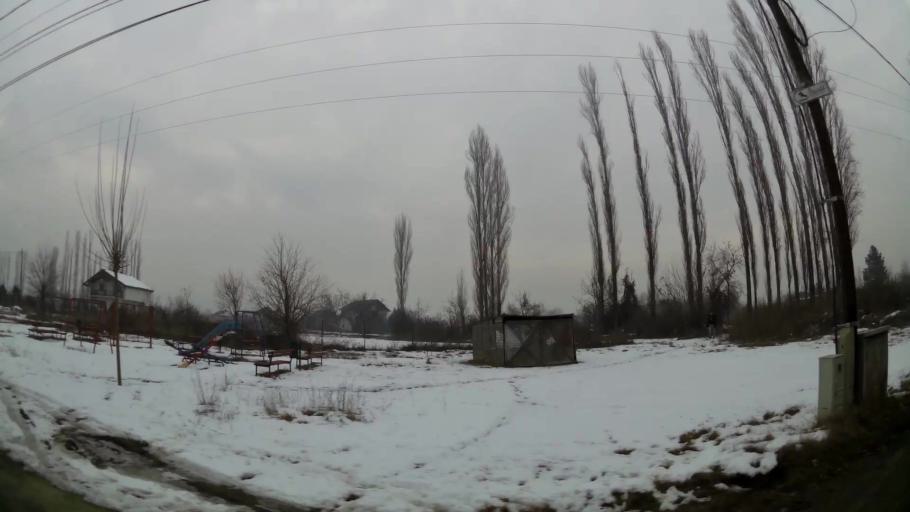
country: MK
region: Saraj
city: Saraj
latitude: 42.0457
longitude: 21.3636
